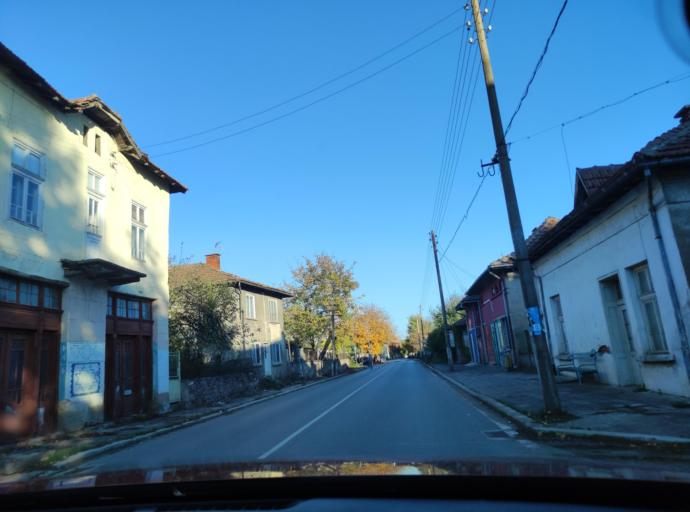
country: BG
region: Montana
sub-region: Obshtina Chiprovtsi
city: Chiprovtsi
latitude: 43.4335
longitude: 22.9757
